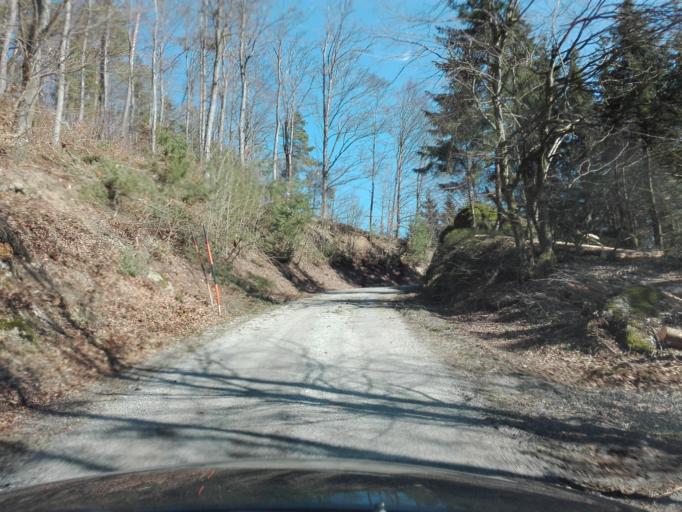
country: AT
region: Upper Austria
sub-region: Politischer Bezirk Perg
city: Bad Kreuzen
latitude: 48.3742
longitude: 14.7638
